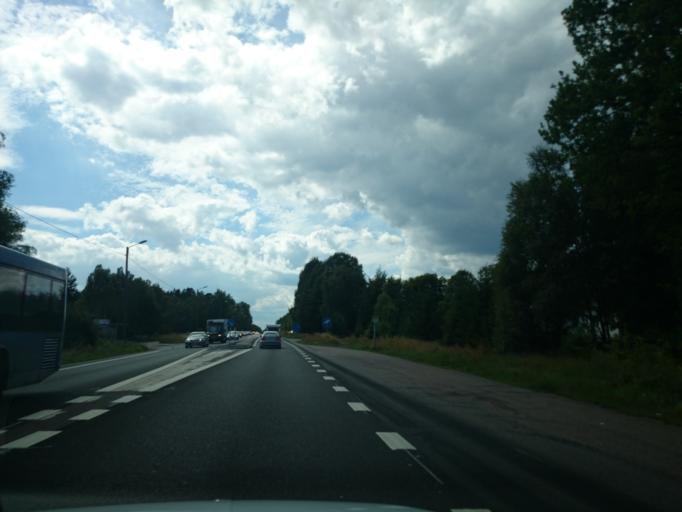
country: SE
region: Kalmar
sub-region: Kalmar Kommun
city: Rinkabyholm
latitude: 56.6514
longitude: 16.2588
